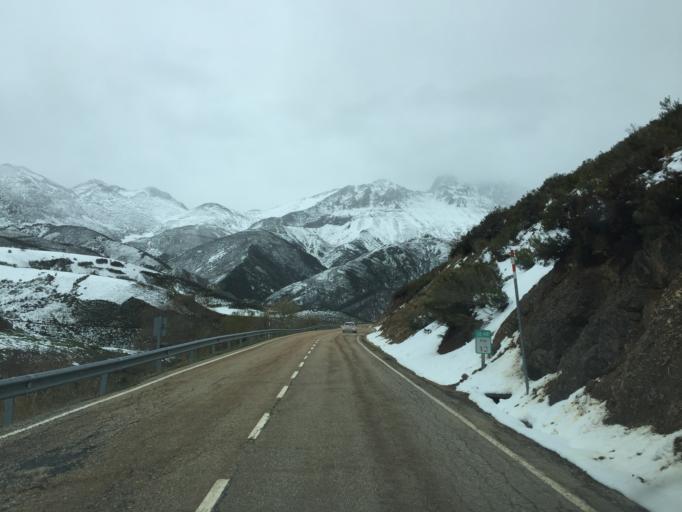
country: ES
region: Castille and Leon
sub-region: Provincia de Leon
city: San Emiliano
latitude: 43.0459
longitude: -6.0175
